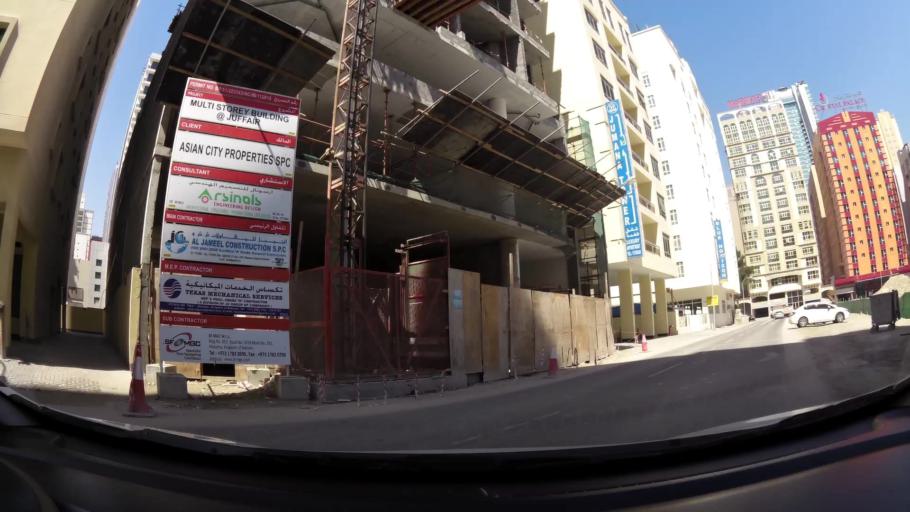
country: BH
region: Manama
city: Manama
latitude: 26.2201
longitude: 50.6088
